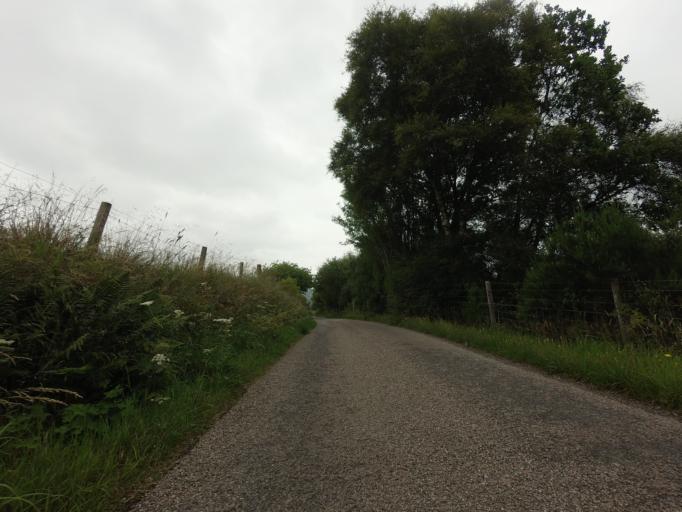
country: GB
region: Scotland
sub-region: Highland
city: Evanton
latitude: 57.9084
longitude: -4.3959
